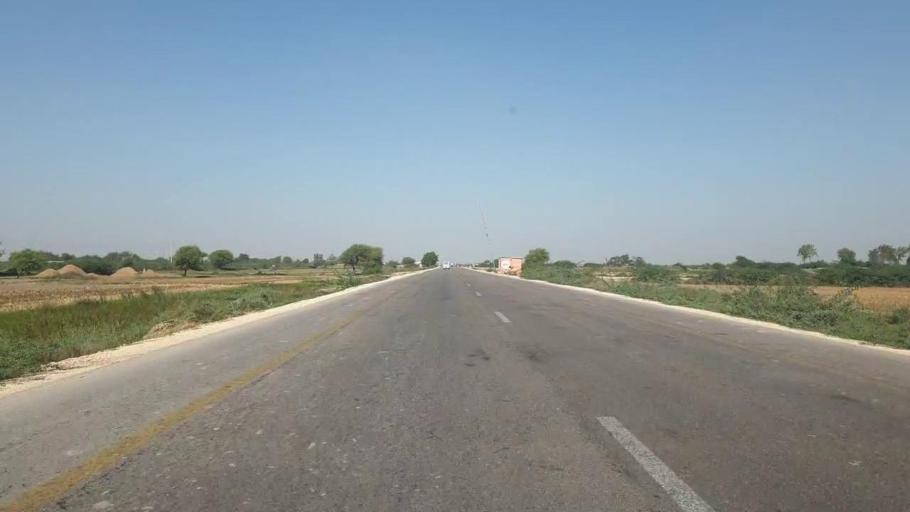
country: PK
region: Sindh
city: Talhar
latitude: 24.8295
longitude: 68.8160
